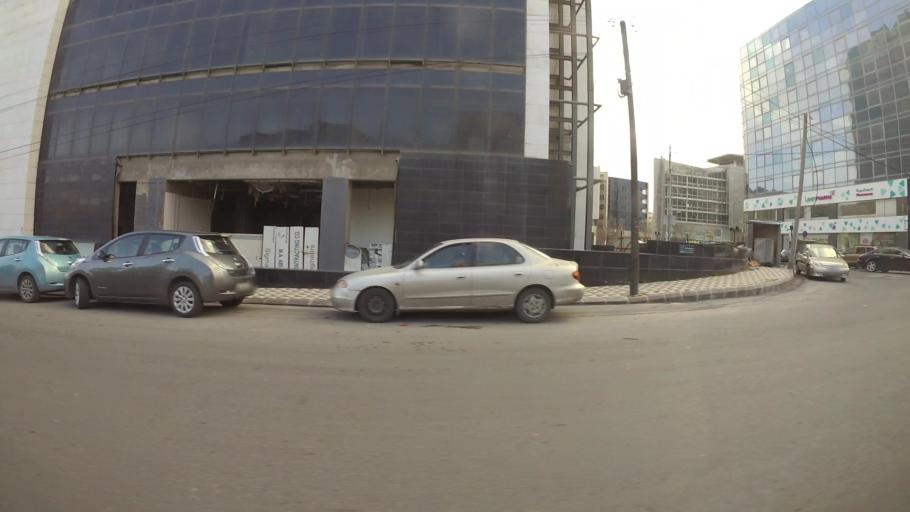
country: JO
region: Amman
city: Wadi as Sir
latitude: 31.9767
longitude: 35.8597
